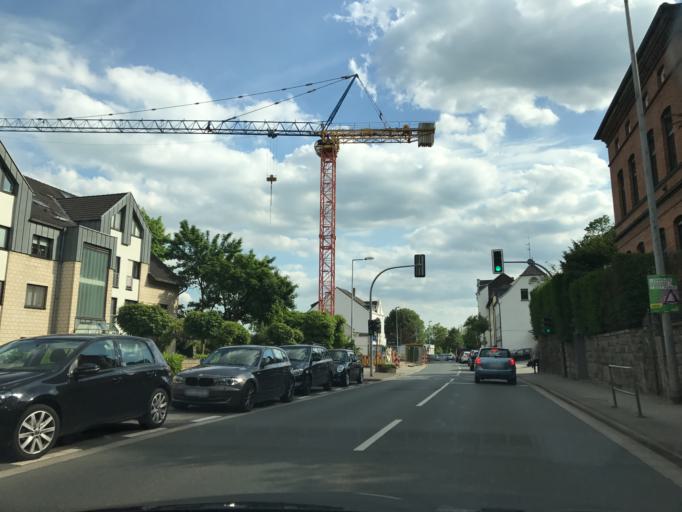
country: DE
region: North Rhine-Westphalia
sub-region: Regierungsbezirk Dusseldorf
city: Muelheim (Ruhr)
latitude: 51.4223
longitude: 6.8726
